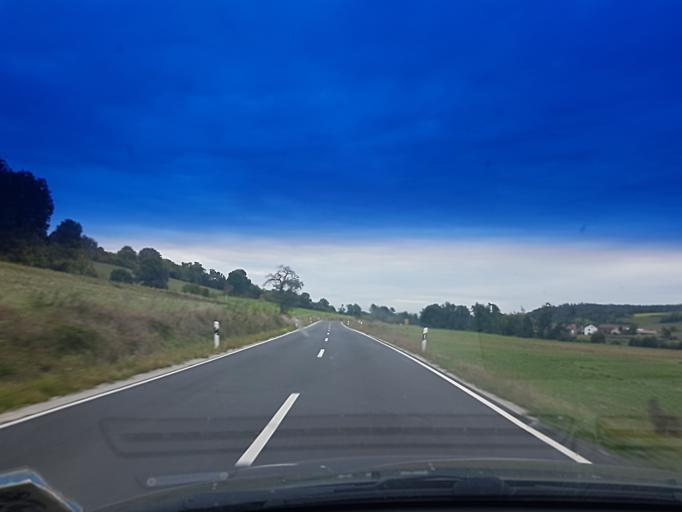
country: DE
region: Bavaria
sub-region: Upper Franconia
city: Burgwindheim
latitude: 49.8320
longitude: 10.5600
